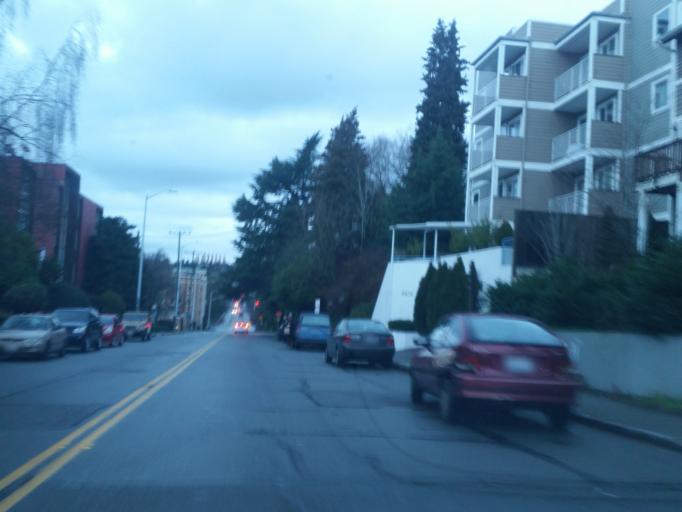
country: US
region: Washington
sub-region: King County
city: Seattle
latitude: 47.6697
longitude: -122.3119
